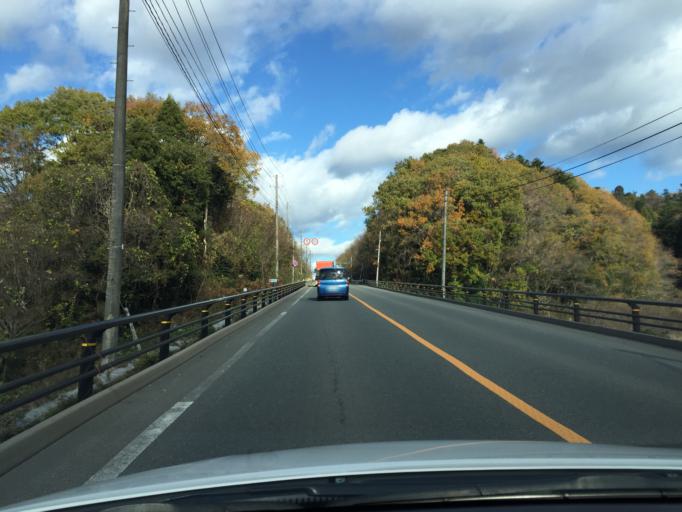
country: JP
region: Fukushima
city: Namie
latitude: 37.4738
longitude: 141.0079
